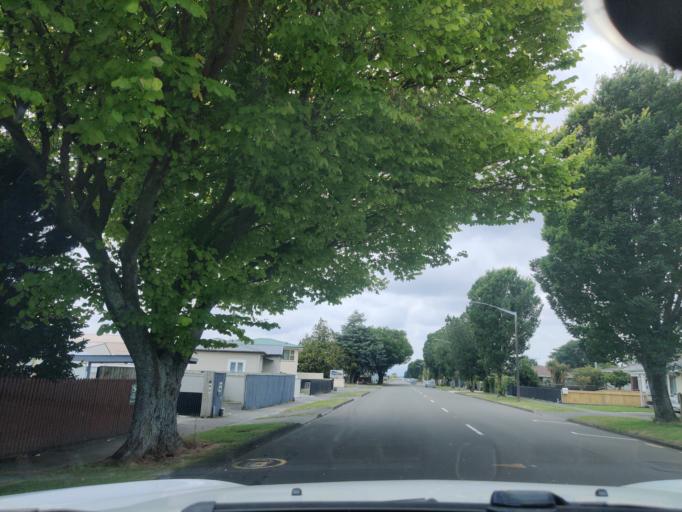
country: NZ
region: Manawatu-Wanganui
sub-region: Palmerston North City
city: Palmerston North
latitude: -40.3505
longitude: 175.5858
